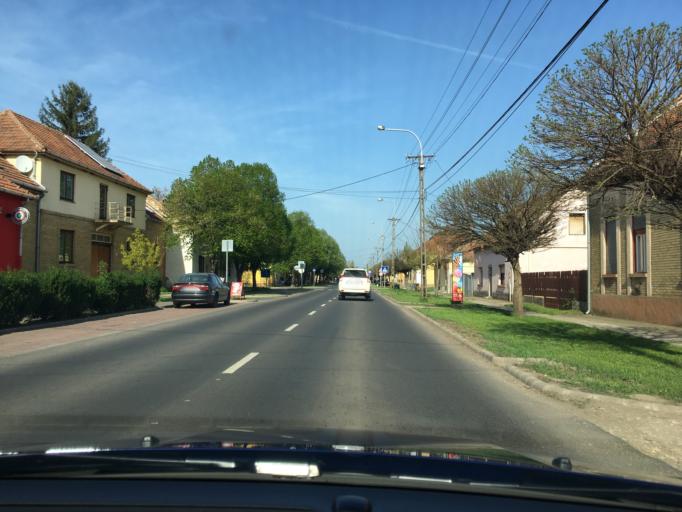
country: HU
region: Bekes
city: Csorvas
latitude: 46.6319
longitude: 20.8243
